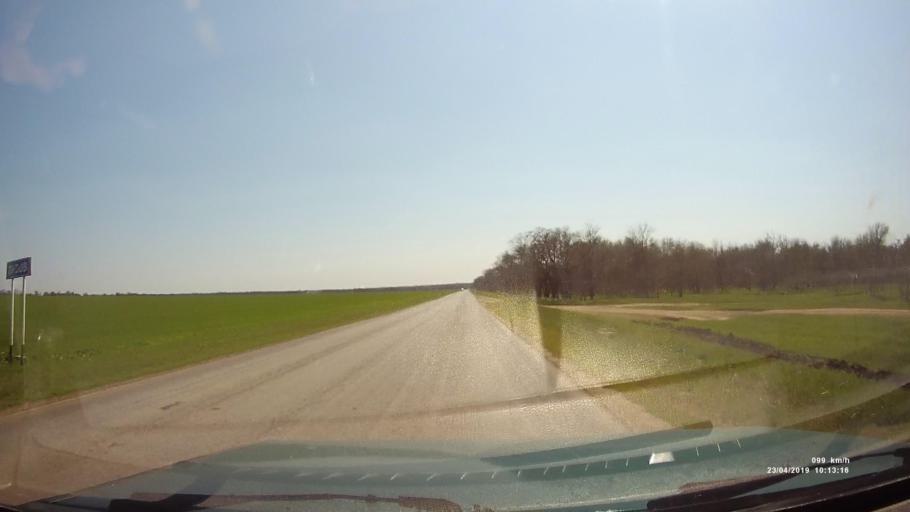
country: RU
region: Rostov
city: Sovetskoye
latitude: 46.6858
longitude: 42.3518
